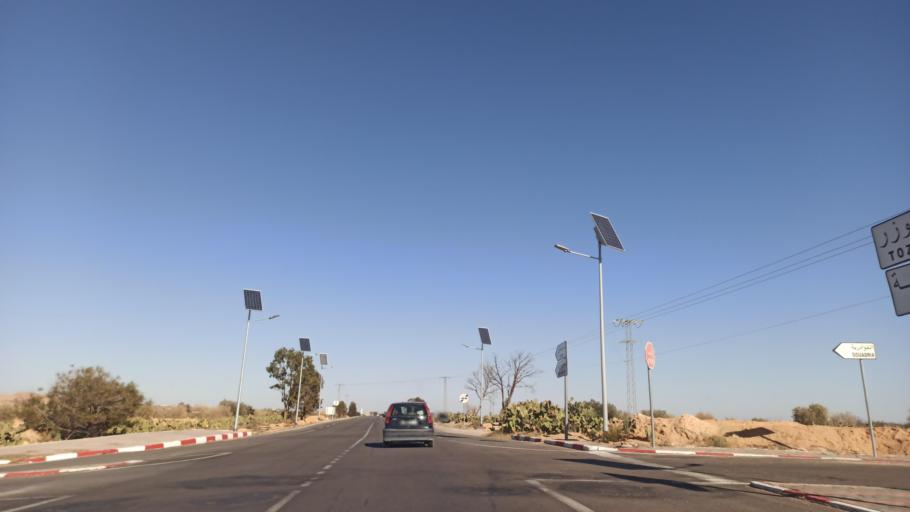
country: TN
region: Sidi Bu Zayd
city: Bi'r al Hufayy
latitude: 34.7257
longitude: 9.0639
